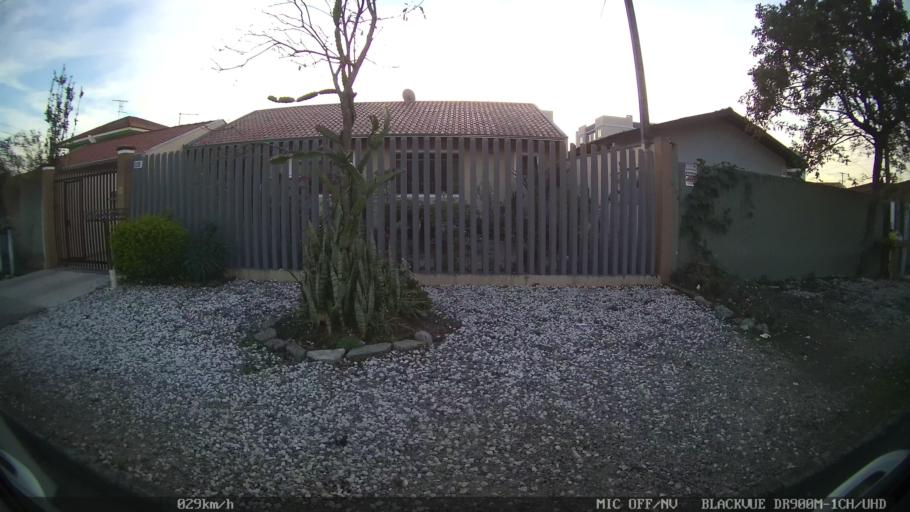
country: BR
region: Parana
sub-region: Pinhais
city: Pinhais
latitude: -25.4426
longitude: -49.1809
